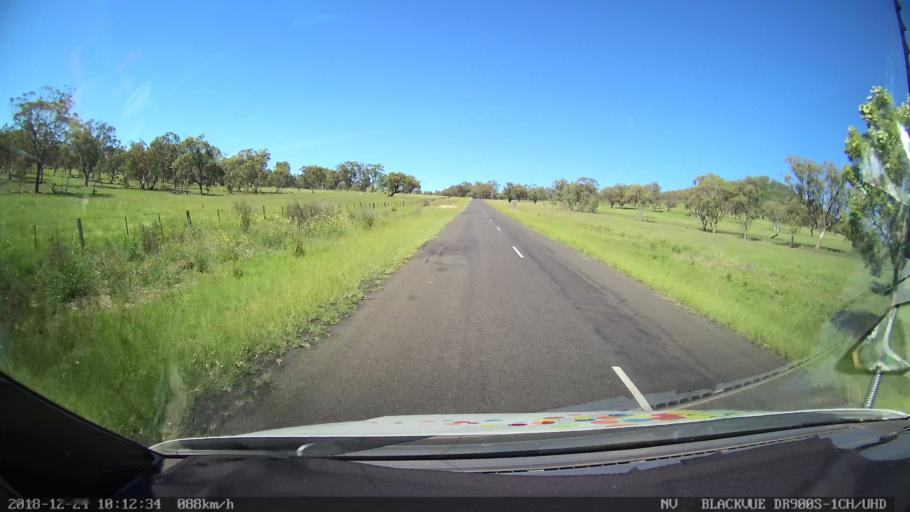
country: AU
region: New South Wales
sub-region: Liverpool Plains
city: Quirindi
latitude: -31.6803
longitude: 150.6466
